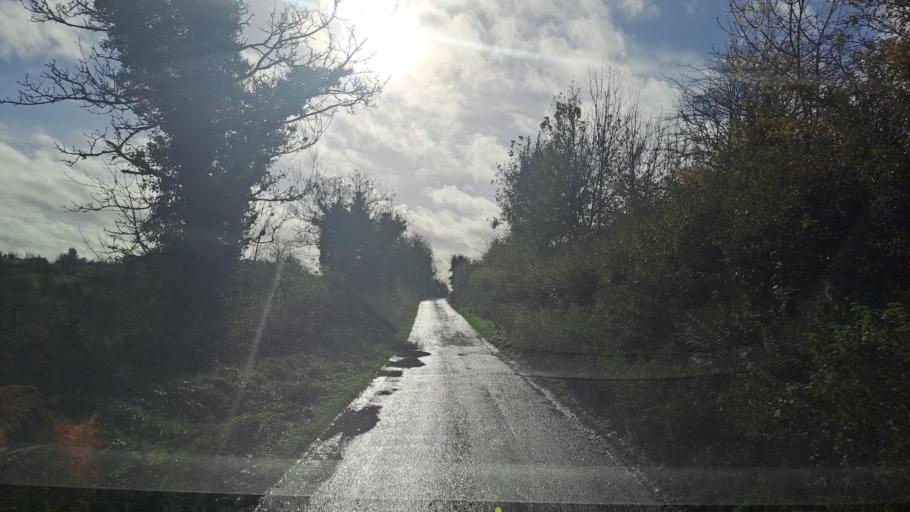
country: IE
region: Ulster
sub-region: An Cabhan
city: Cootehill
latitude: 54.0176
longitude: -7.0362
